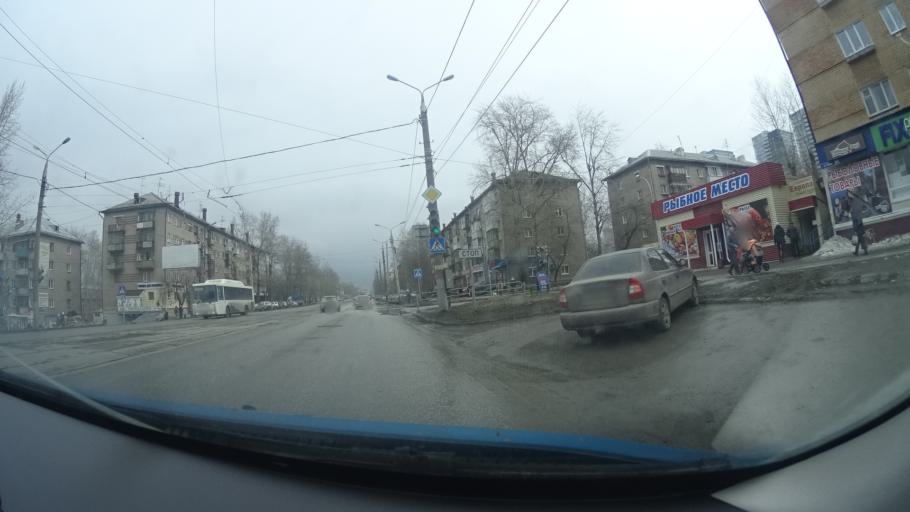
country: RU
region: Perm
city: Kondratovo
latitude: 57.9716
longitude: 56.1637
